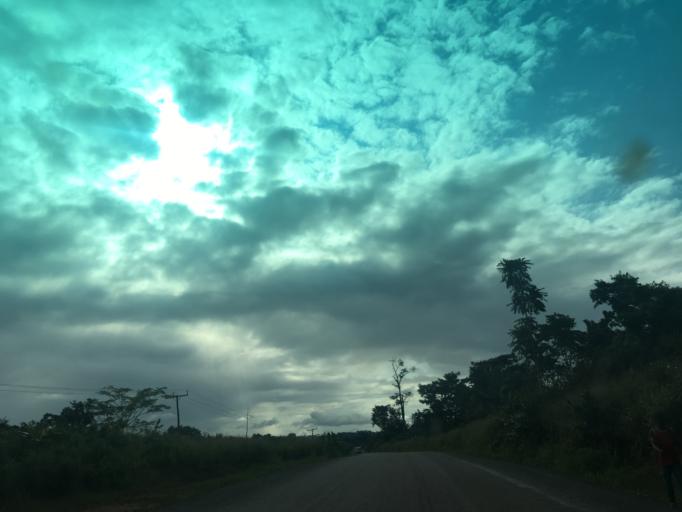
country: GH
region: Western
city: Bibiani
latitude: 6.1183
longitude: -2.3271
